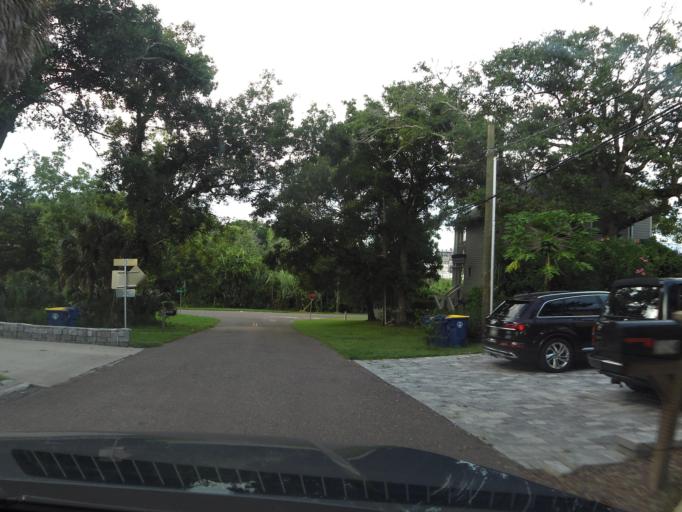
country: US
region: Florida
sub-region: Nassau County
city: Fernandina Beach
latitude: 30.6755
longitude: -81.4606
